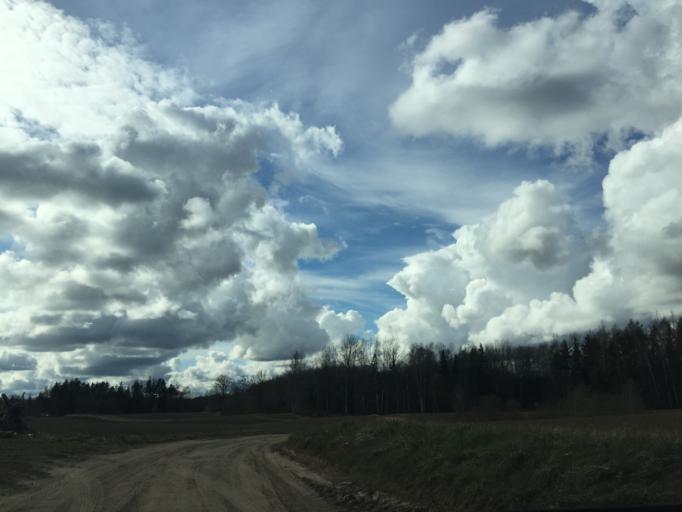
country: LV
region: Burtnieki
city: Matisi
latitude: 57.6180
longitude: 24.9961
